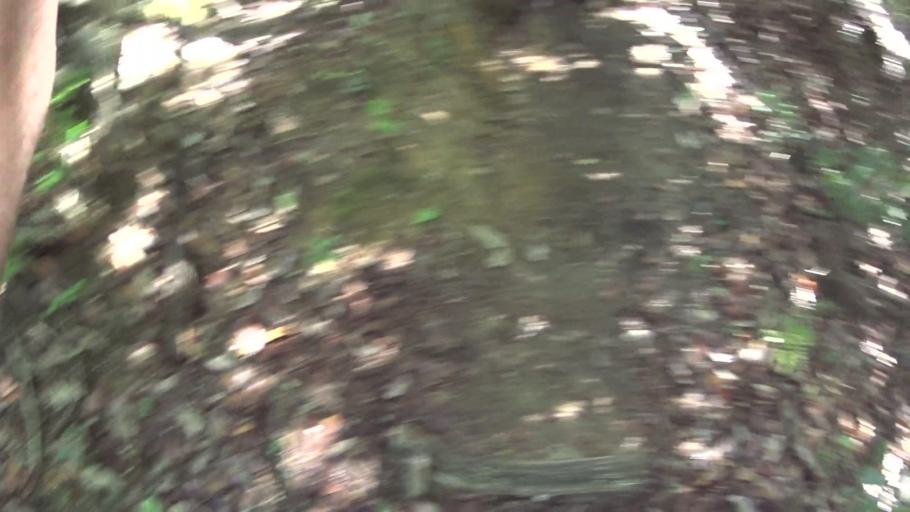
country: JP
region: Kyoto
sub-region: Kyoto-shi
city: Kamigyo-ku
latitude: 35.0415
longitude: 135.7945
